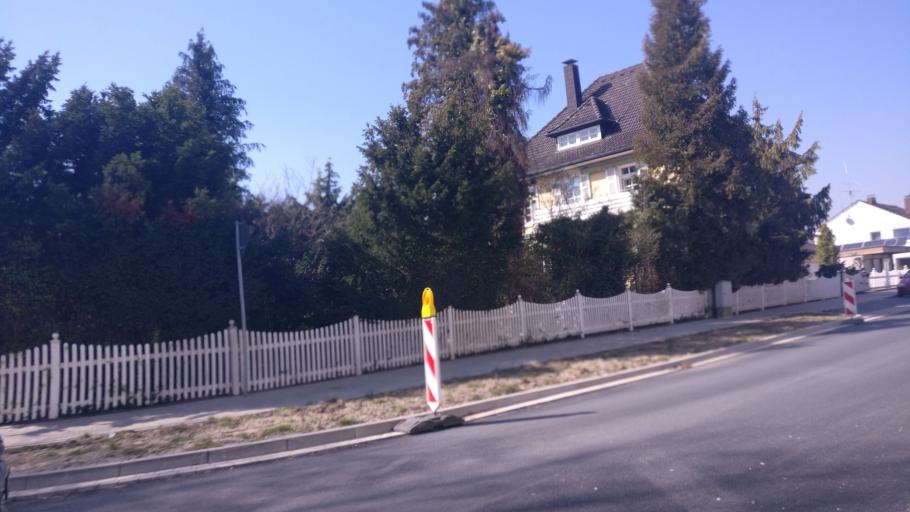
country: DE
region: North Rhine-Westphalia
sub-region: Regierungsbezirk Detmold
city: Lage
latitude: 51.9916
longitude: 8.7853
